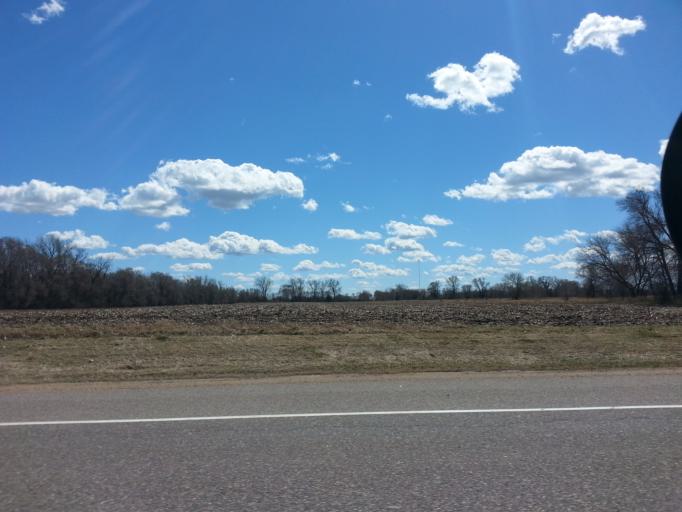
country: US
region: Minnesota
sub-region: Dakota County
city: Rosemount
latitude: 44.7172
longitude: -93.0657
